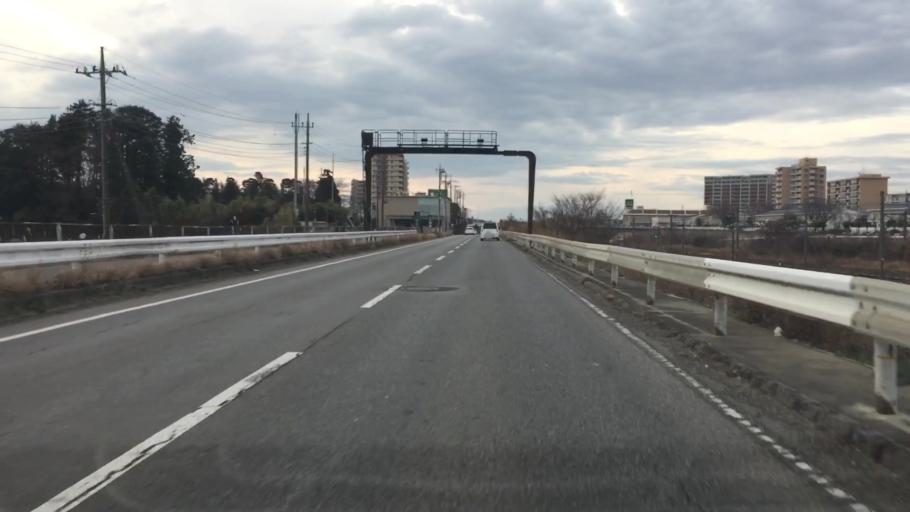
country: JP
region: Chiba
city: Shiroi
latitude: 35.7841
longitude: 140.0390
